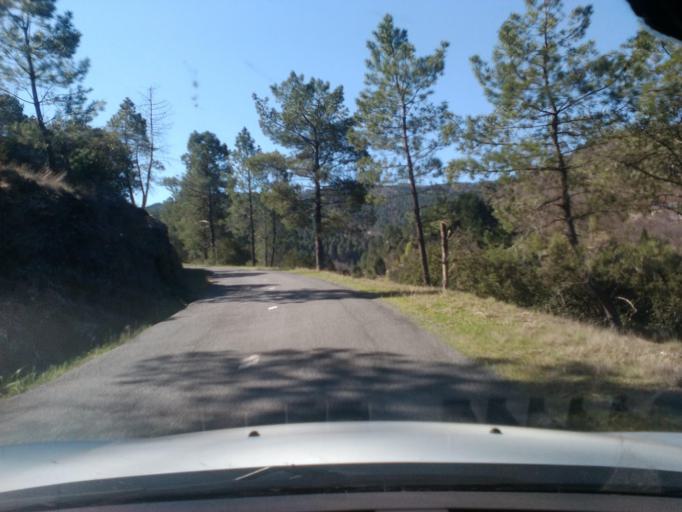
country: FR
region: Languedoc-Roussillon
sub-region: Departement du Gard
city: Valleraugue
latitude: 44.1729
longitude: 3.7511
